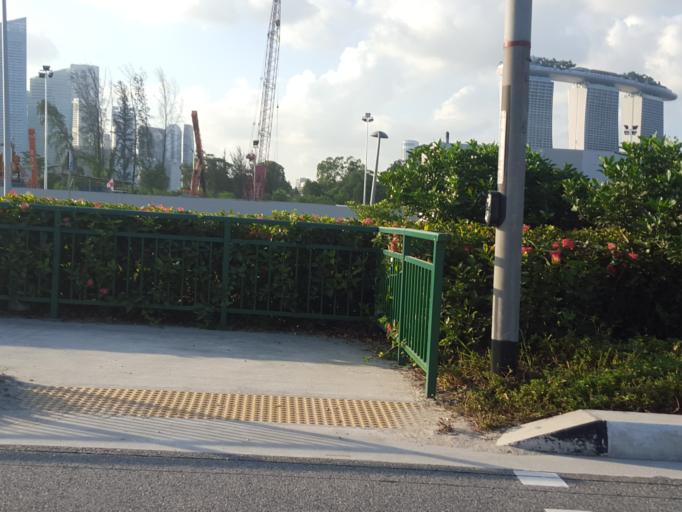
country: SG
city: Singapore
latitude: 1.2729
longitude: 103.8636
